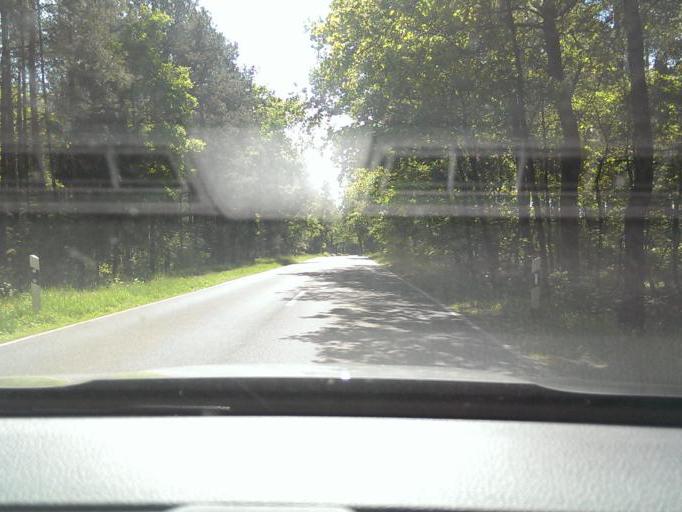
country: DE
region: Lower Saxony
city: Winsen (Aller)
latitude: 52.6892
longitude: 9.8638
